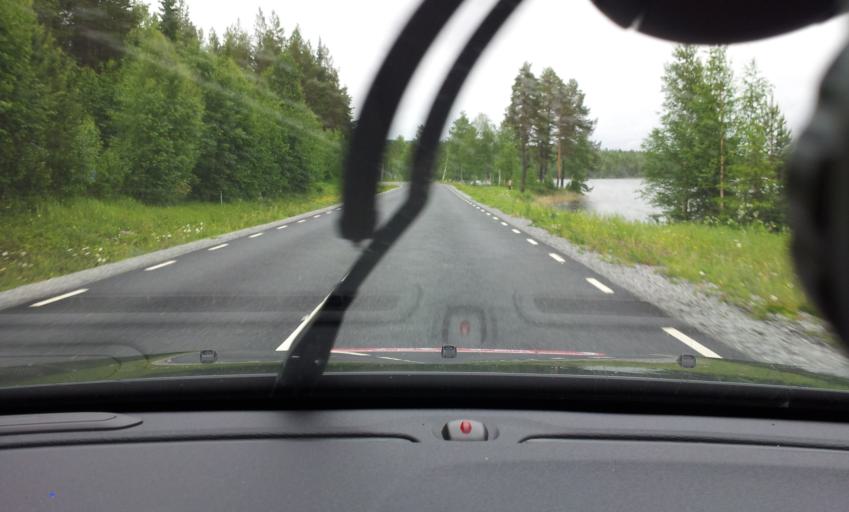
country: SE
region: Jaemtland
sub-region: OEstersunds Kommun
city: Lit
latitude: 63.7428
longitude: 14.7955
